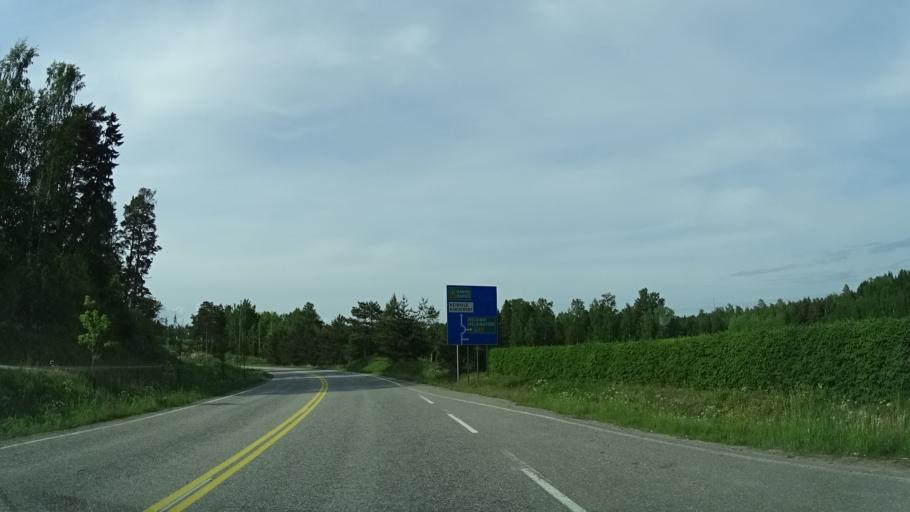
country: FI
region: Uusimaa
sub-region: Helsinki
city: Kirkkonummi
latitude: 60.1163
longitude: 24.4822
